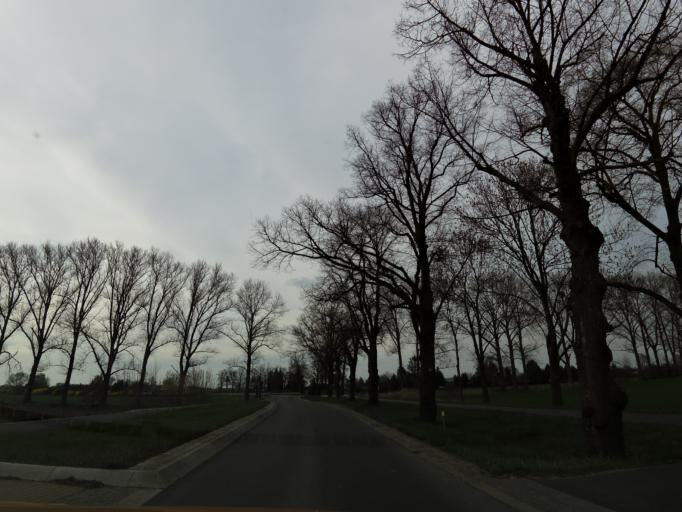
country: DE
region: Brandenburg
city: Mittenwalde
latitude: 52.2740
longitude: 13.5375
